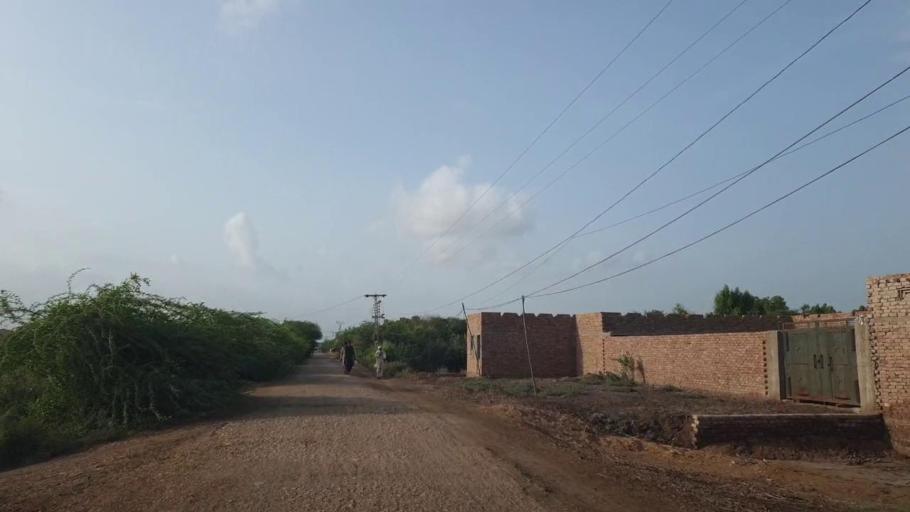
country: PK
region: Sindh
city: Tando Bago
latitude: 24.6439
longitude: 69.1117
